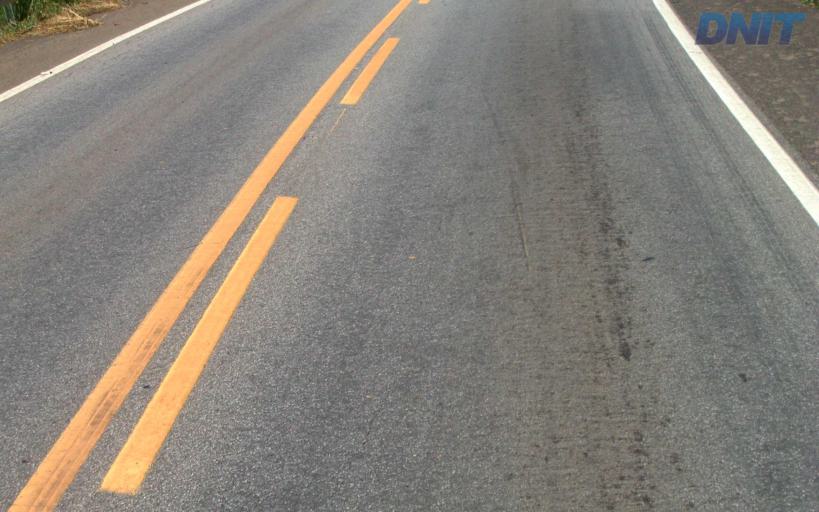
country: BR
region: Minas Gerais
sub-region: Ipaba
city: Ipaba
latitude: -19.3938
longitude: -42.4832
